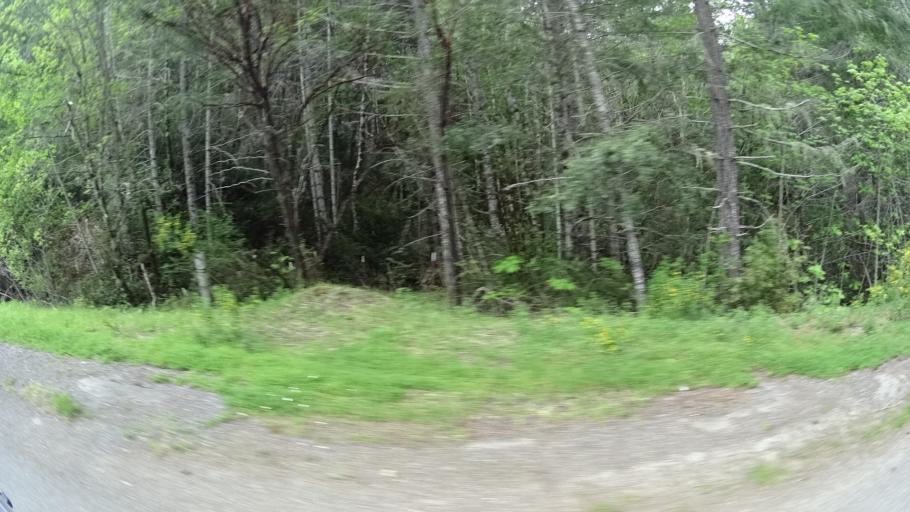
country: US
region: California
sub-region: Humboldt County
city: Redway
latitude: 40.1443
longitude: -123.6307
